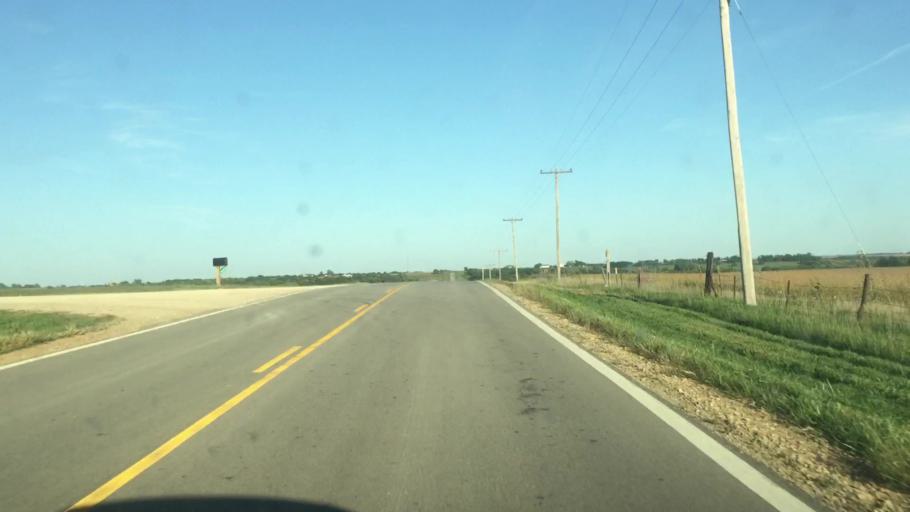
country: US
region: Kansas
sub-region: Brown County
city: Horton
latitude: 39.5876
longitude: -95.5724
